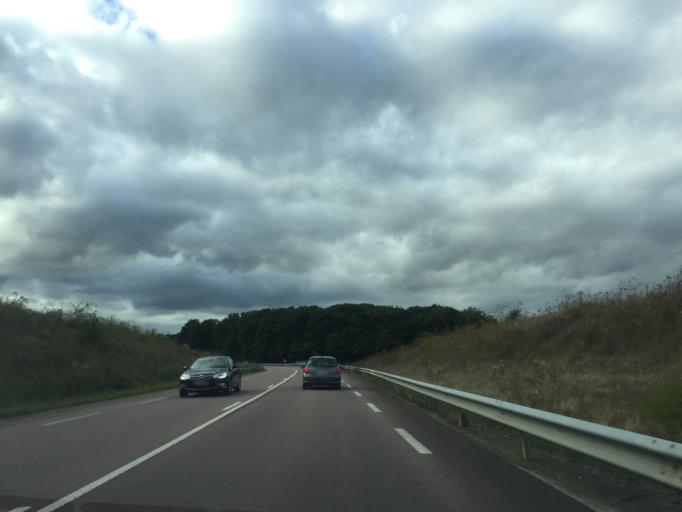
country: FR
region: Lorraine
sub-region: Departement des Vosges
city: Chatenois
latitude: 48.2977
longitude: 5.8830
